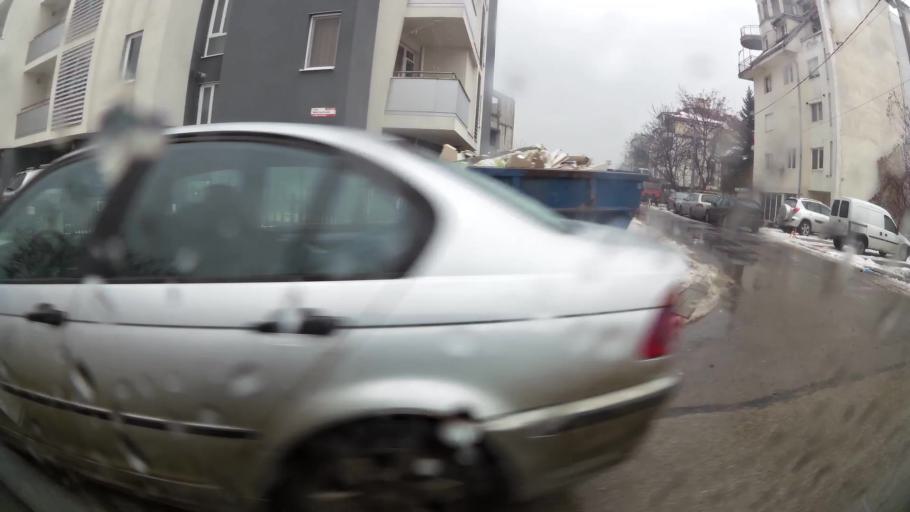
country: BG
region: Sofia-Capital
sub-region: Stolichna Obshtina
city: Sofia
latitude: 42.6808
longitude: 23.2596
